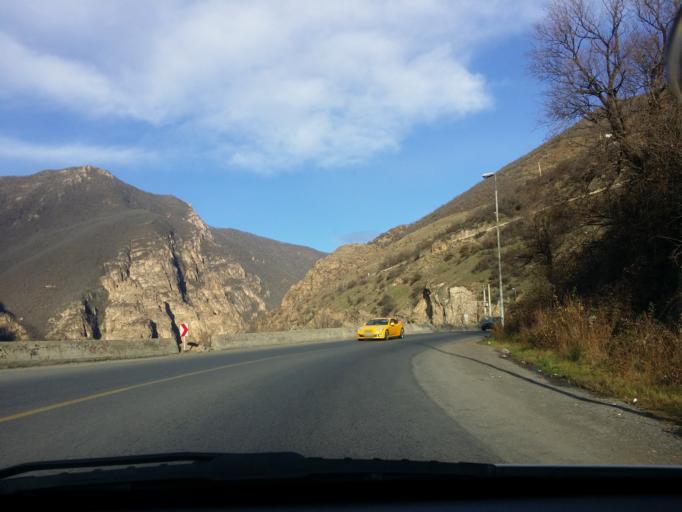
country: IR
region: Mazandaran
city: Chalus
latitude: 36.2666
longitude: 51.2591
